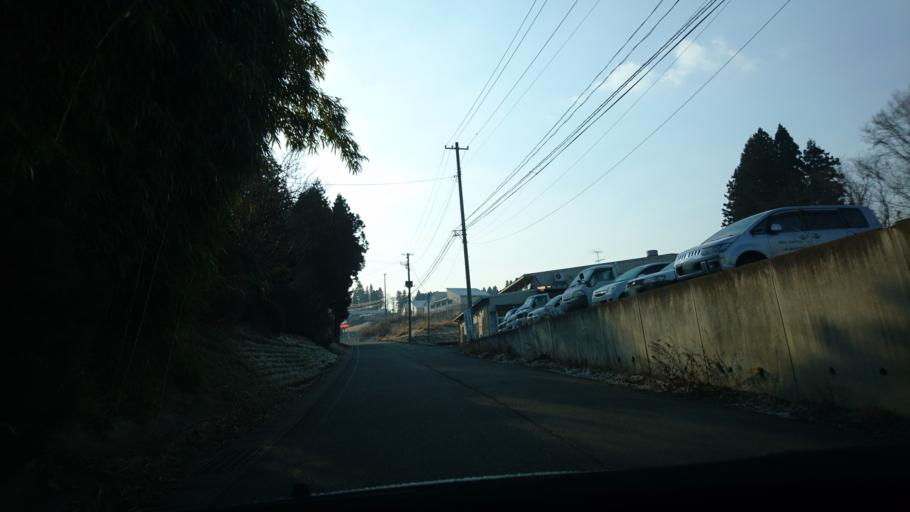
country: JP
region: Iwate
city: Ichinoseki
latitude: 38.9235
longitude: 141.3484
